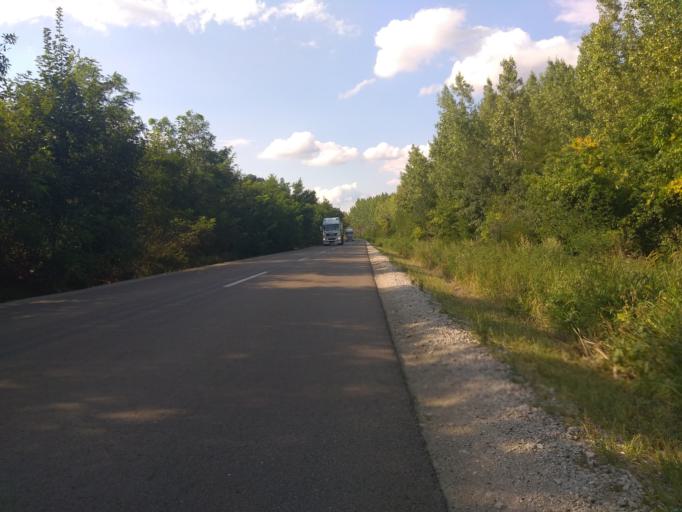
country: HU
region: Borsod-Abauj-Zemplen
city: Hejobaba
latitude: 47.8870
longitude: 20.8972
